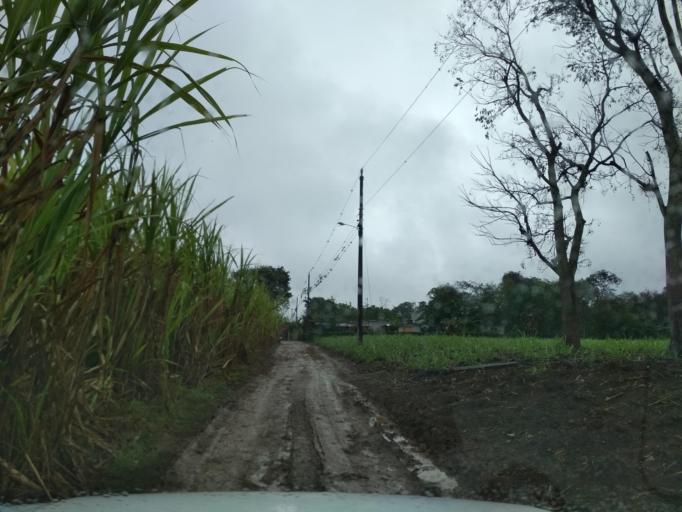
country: MX
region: Veracruz
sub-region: Amatlan de los Reyes
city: Centro de Readaptacion Social
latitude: 18.8336
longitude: -96.9318
